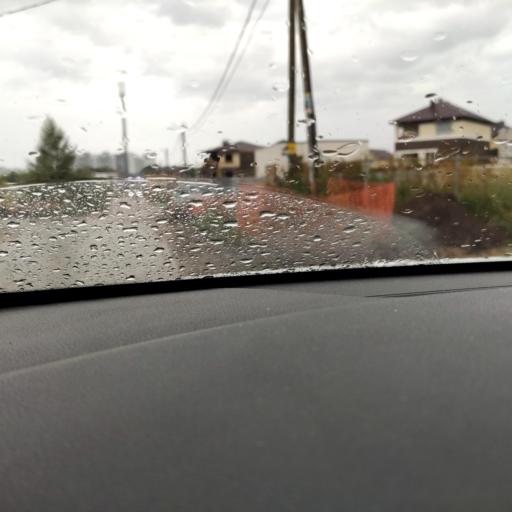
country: RU
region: Tatarstan
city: Vysokaya Gora
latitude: 55.7883
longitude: 49.2599
